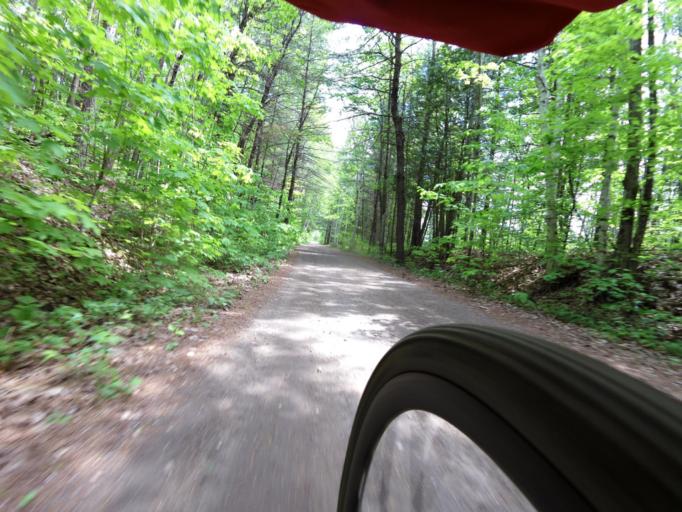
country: CA
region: Ontario
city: Renfrew
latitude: 45.2080
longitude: -76.6908
